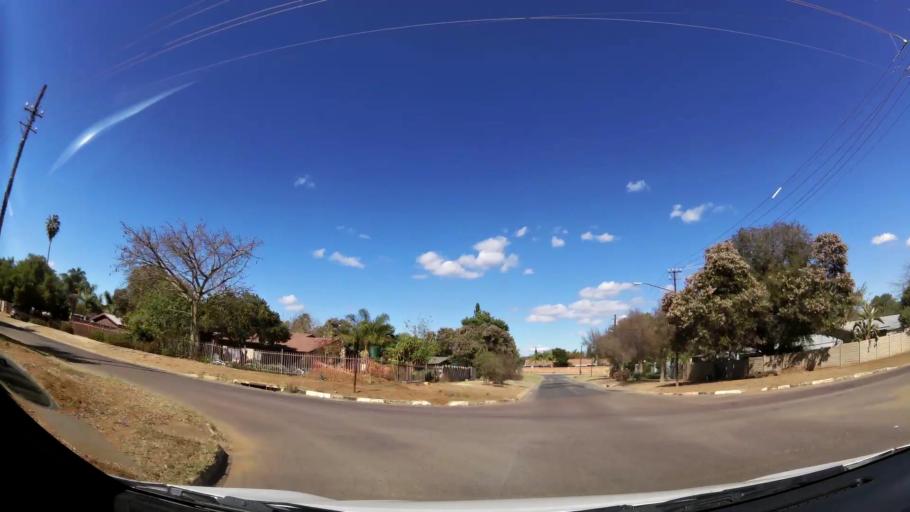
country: ZA
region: Limpopo
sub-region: Capricorn District Municipality
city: Polokwane
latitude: -23.9157
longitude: 29.4721
